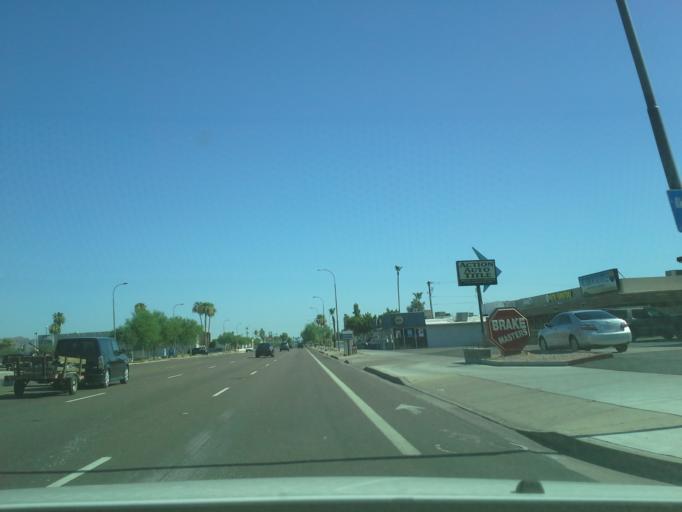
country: US
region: Arizona
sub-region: Maricopa County
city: Scottsdale
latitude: 33.4686
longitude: -111.9261
